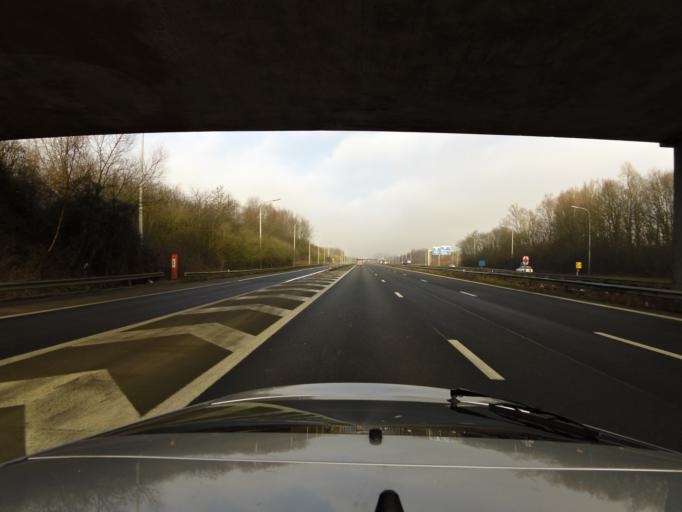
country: BE
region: Flanders
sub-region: Provincie West-Vlaanderen
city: Wevelgem
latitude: 50.8243
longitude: 3.1931
